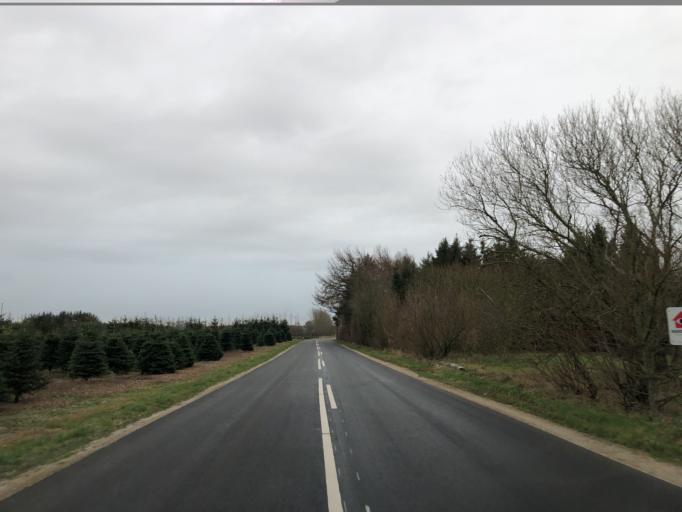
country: DK
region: Central Jutland
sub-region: Holstebro Kommune
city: Vinderup
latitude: 56.3921
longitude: 8.8241
